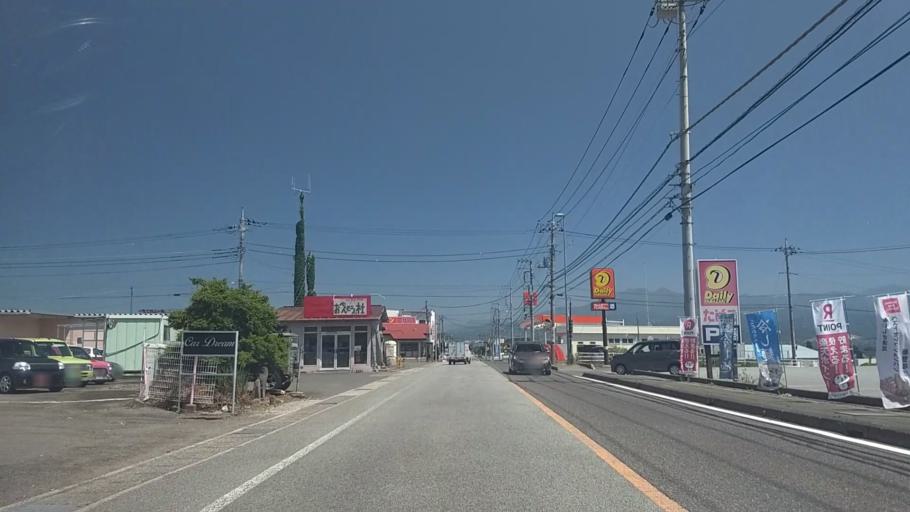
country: JP
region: Yamanashi
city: Nirasaki
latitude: 35.6669
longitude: 138.4646
